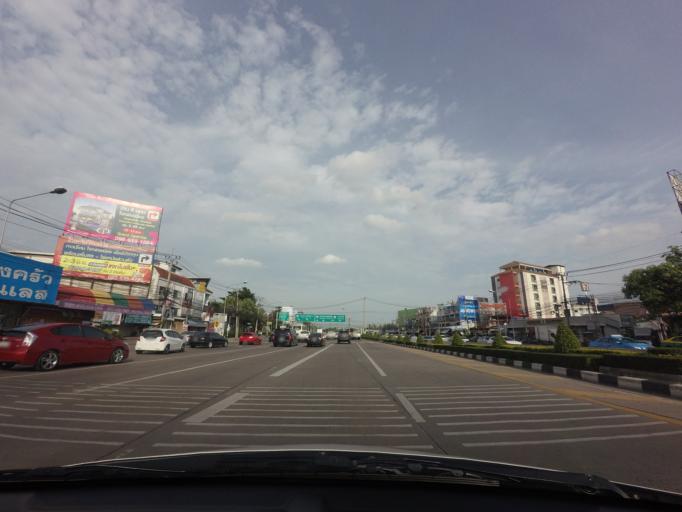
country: TH
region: Bangkok
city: Bueng Kum
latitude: 13.8111
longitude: 100.6487
